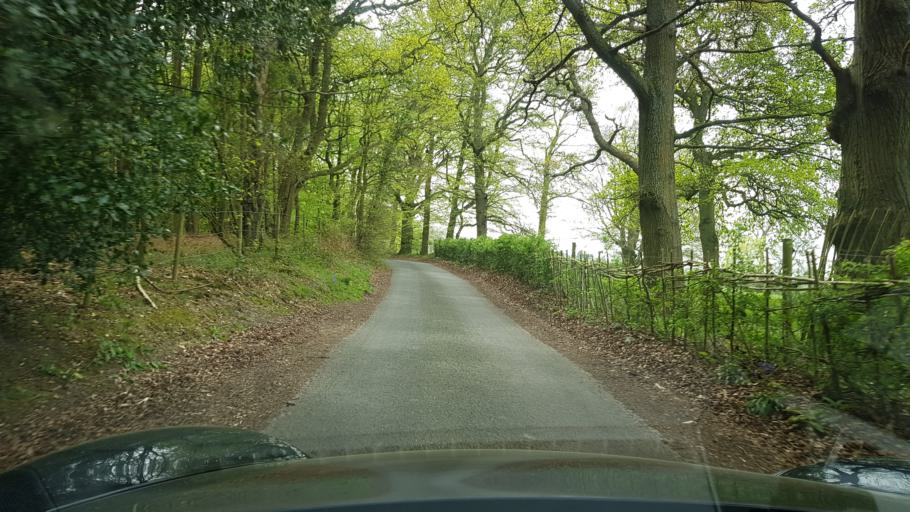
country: GB
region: England
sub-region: Surrey
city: East Horsley
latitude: 51.2397
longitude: -0.4510
